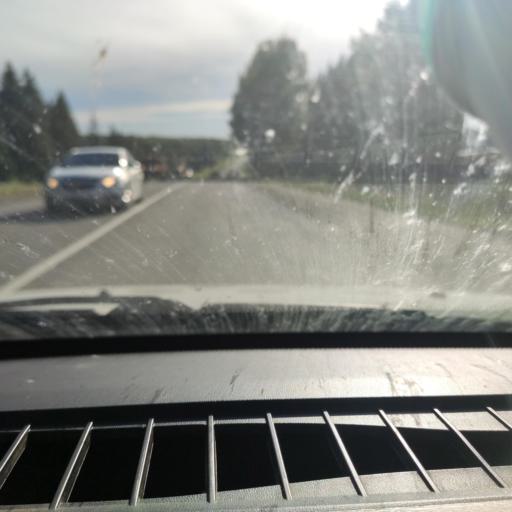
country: RU
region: Kirov
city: Vakhrushi
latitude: 58.6768
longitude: 49.9680
